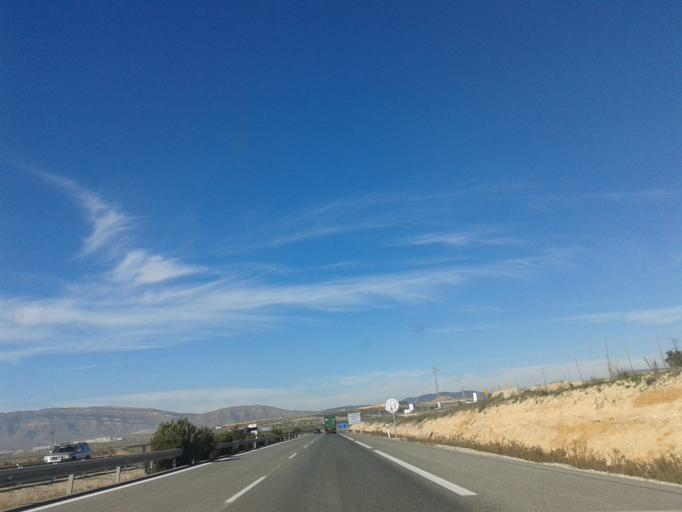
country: ES
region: Castille-La Mancha
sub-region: Provincia de Albacete
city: Caudete
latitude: 38.7011
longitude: -0.9211
